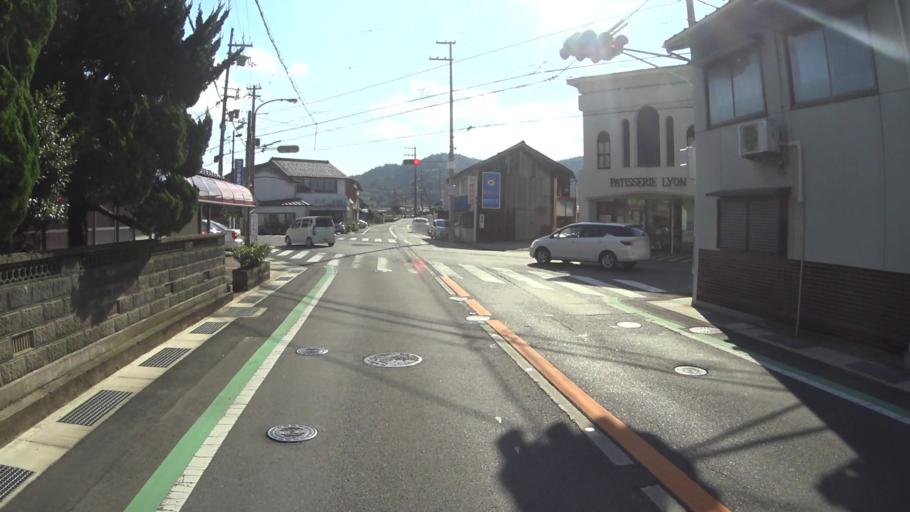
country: JP
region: Kyoto
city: Miyazu
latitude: 35.6782
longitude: 135.0285
